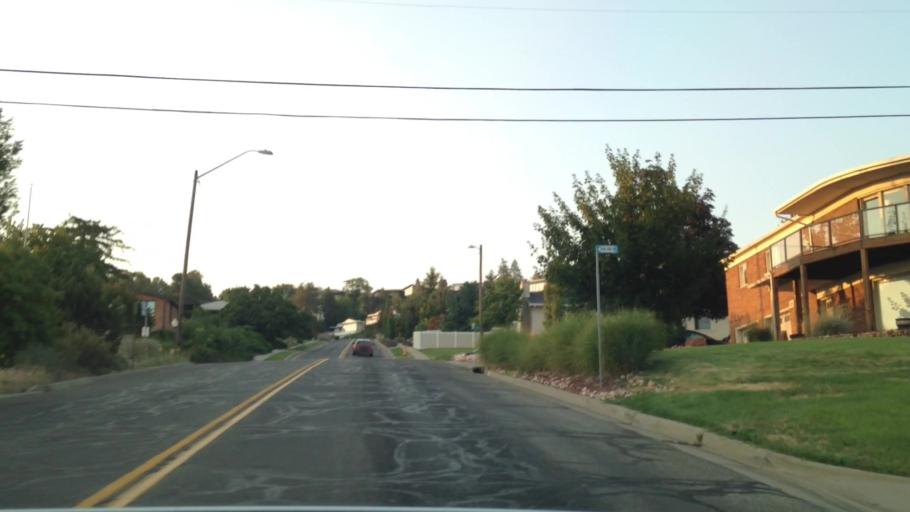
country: US
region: Utah
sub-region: Salt Lake County
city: Salt Lake City
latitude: 40.7836
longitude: -111.8715
